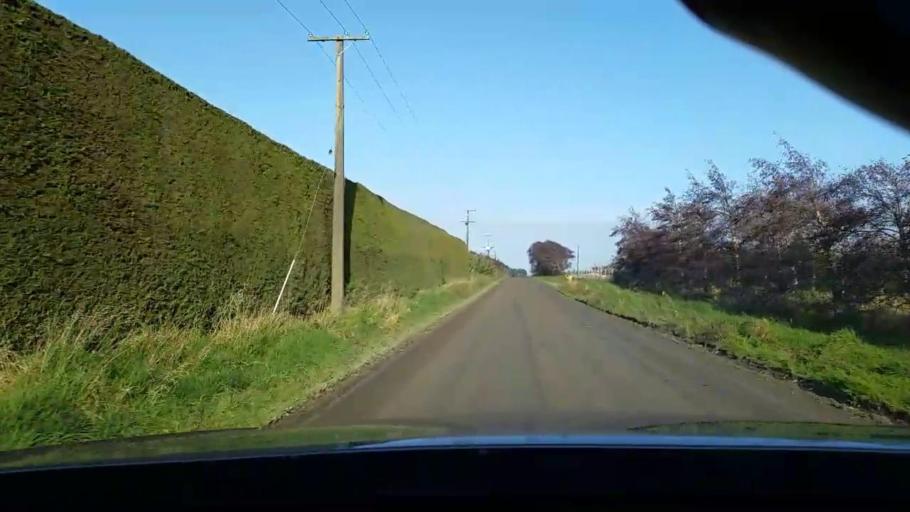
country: NZ
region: Southland
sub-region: Invercargill City
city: Invercargill
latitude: -46.3014
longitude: 168.3033
